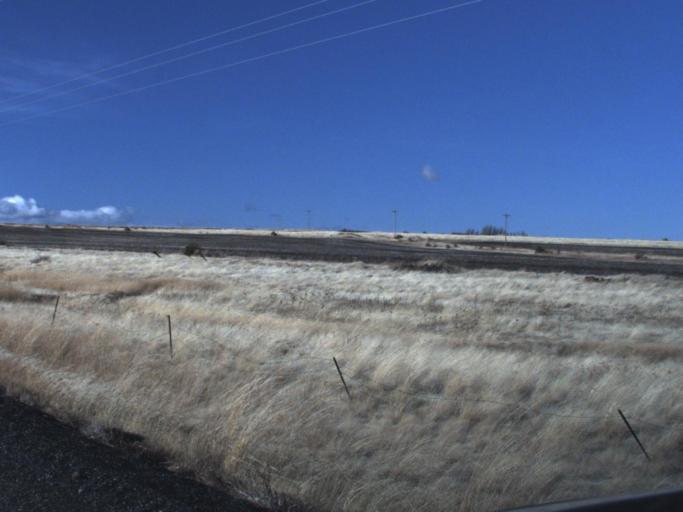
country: US
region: Washington
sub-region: Asotin County
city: Asotin
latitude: 46.1615
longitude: -117.1024
